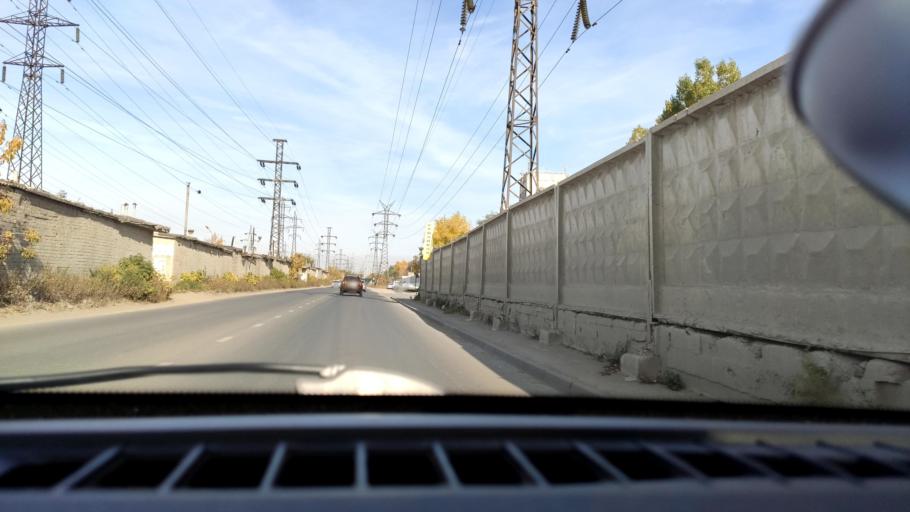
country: RU
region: Samara
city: Petra-Dubrava
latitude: 53.2485
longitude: 50.2935
